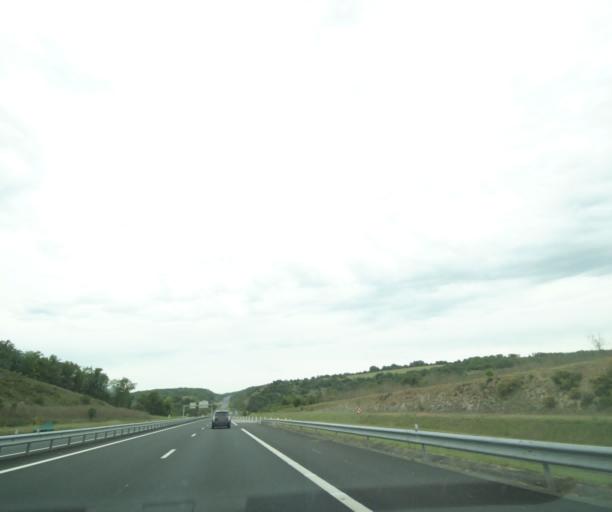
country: FR
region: Midi-Pyrenees
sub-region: Departement du Lot
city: Souillac
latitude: 44.8986
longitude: 1.5026
